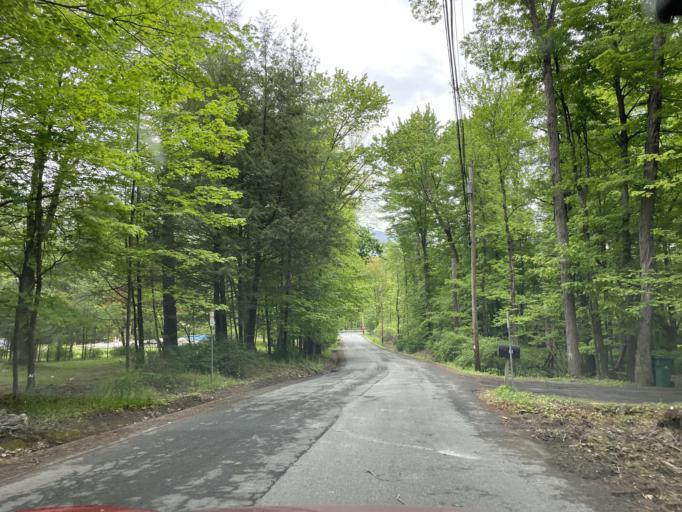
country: US
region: New York
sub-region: Ulster County
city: Woodstock
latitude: 42.0352
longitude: -74.1183
